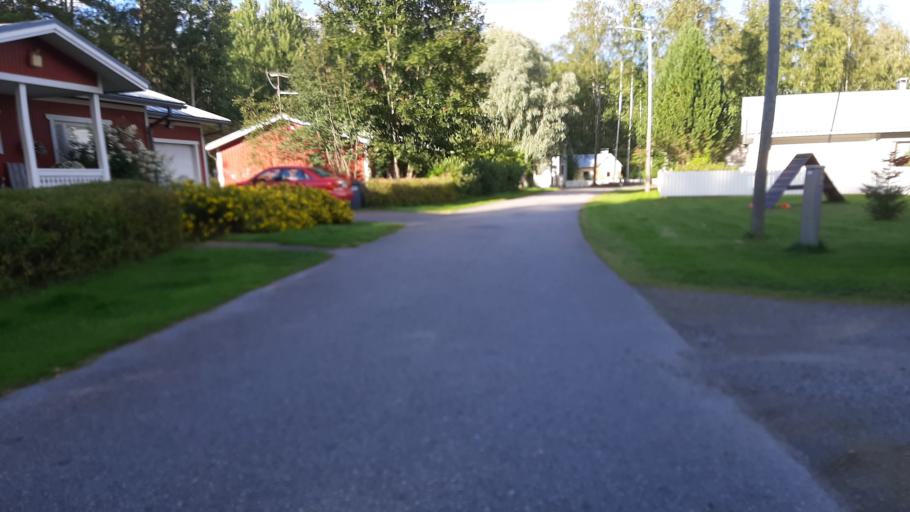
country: FI
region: North Karelia
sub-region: Joensuu
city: Joensuu
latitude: 62.6196
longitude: 29.7828
